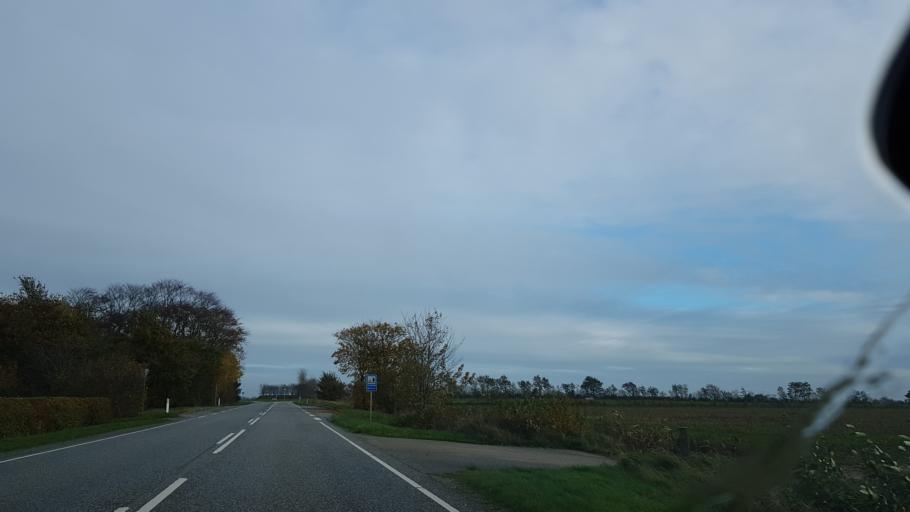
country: DK
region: South Denmark
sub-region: Haderslev Kommune
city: Gram
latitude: 55.2314
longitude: 8.9565
